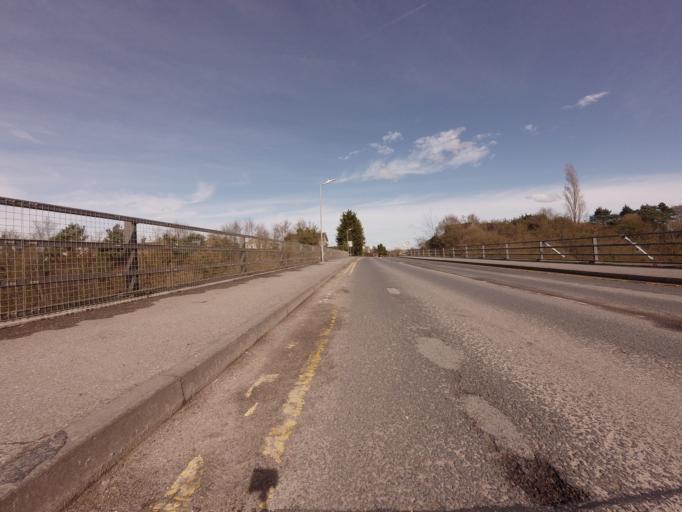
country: GB
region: England
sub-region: Kent
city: Swanley
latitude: 51.3899
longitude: 0.1680
